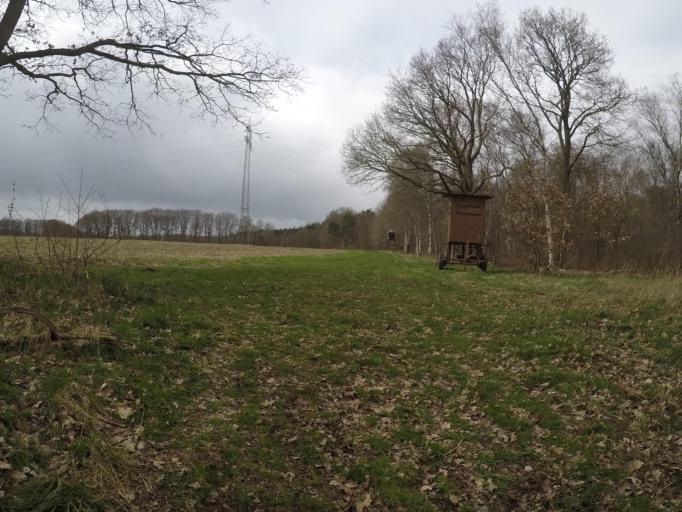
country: DE
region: Lower Saxony
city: Elmlohe
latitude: 53.6237
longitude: 8.6791
